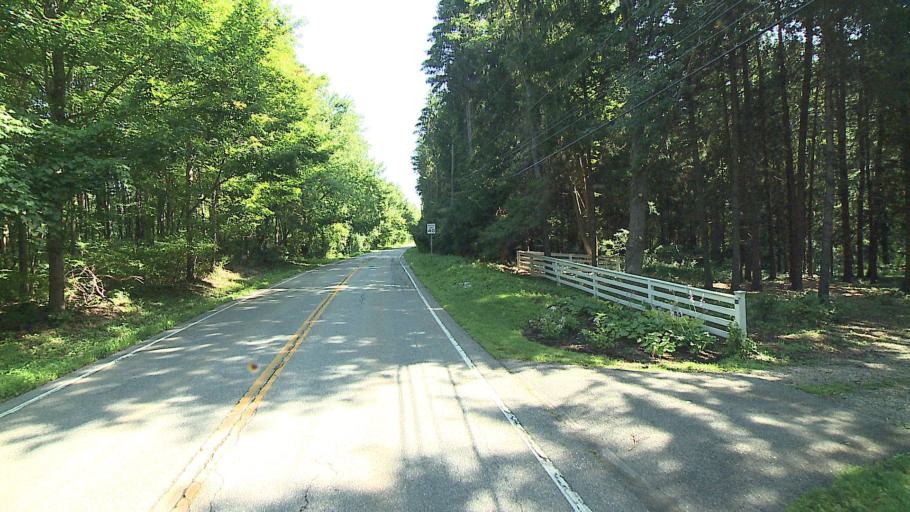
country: US
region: Connecticut
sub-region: Litchfield County
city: Kent
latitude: 41.8594
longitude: -73.4899
